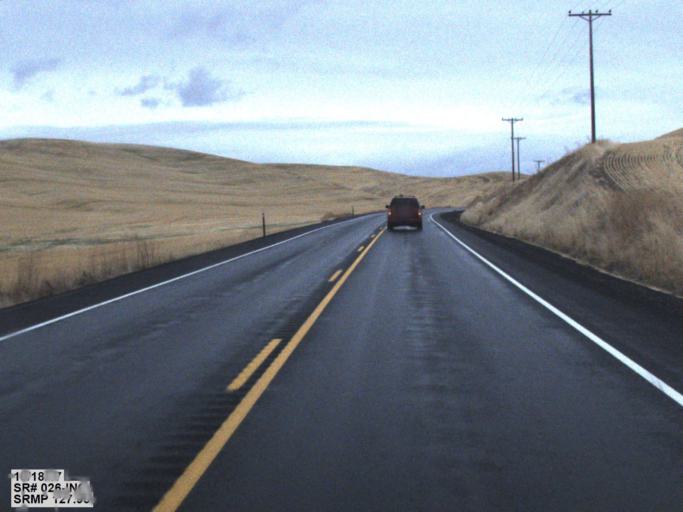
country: US
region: Washington
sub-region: Whitman County
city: Colfax
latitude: 46.8563
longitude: -117.4621
